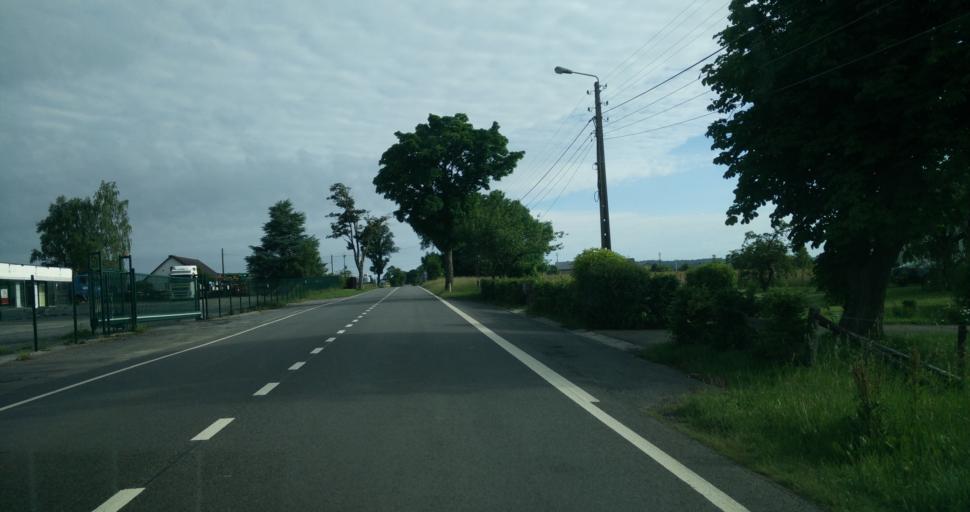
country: BE
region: Wallonia
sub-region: Province du Luxembourg
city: Houffalize
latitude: 50.1556
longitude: 5.7837
